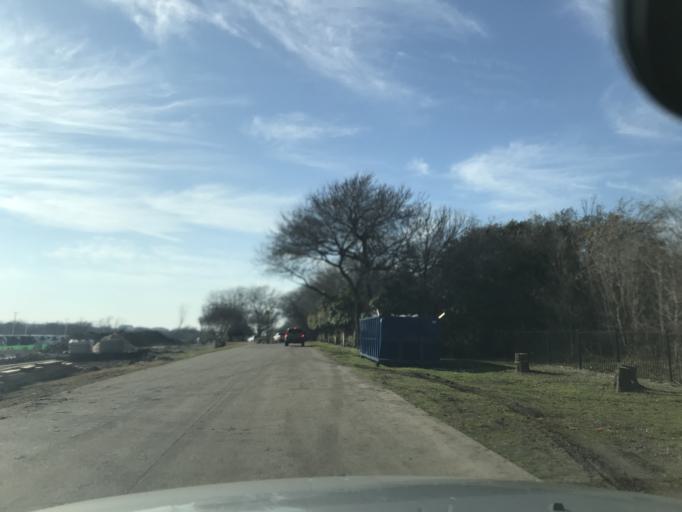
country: US
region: Texas
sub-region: Collin County
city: Frisco
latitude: 33.0948
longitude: -96.8247
